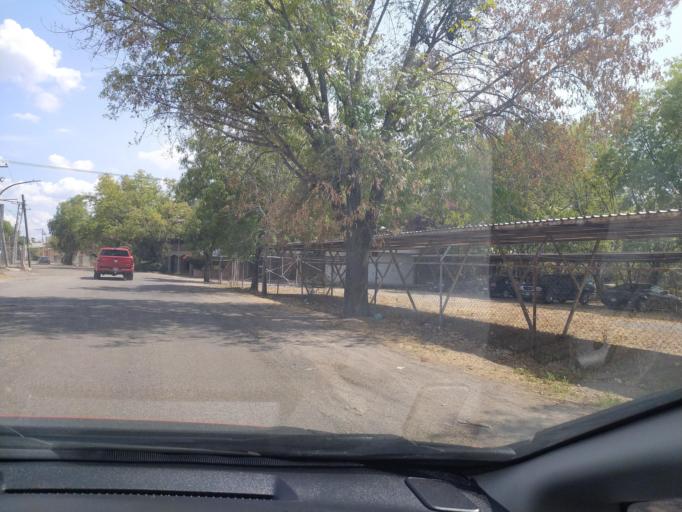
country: MX
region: Guanajuato
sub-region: San Francisco del Rincon
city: Estacion de San Francisco
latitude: 21.0281
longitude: -101.8400
